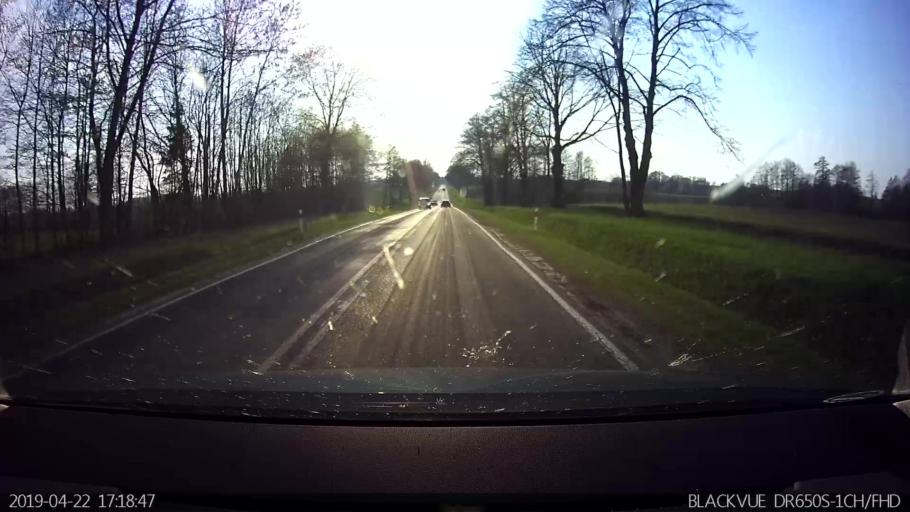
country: PL
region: Masovian Voivodeship
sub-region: Powiat sokolowski
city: Repki
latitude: 52.3849
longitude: 22.4070
